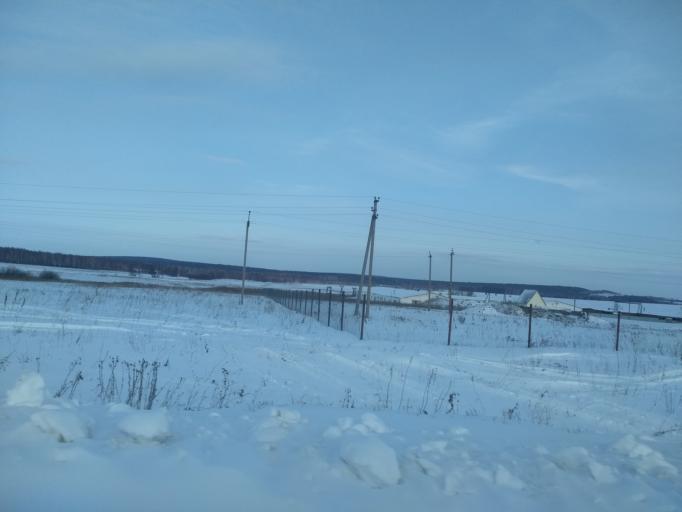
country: RU
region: Bashkortostan
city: Iglino
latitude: 54.7756
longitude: 56.5398
